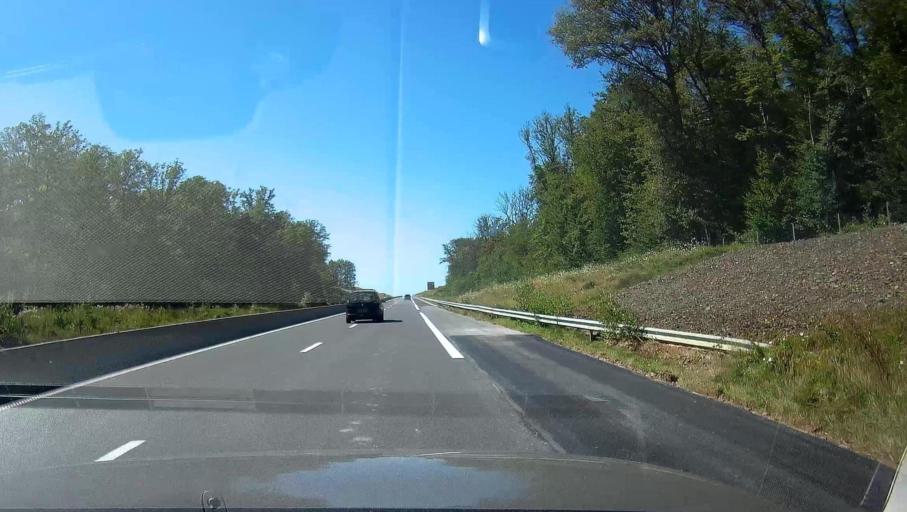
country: FR
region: Champagne-Ardenne
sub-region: Departement des Ardennes
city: Rimogne
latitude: 49.7890
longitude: 4.5619
